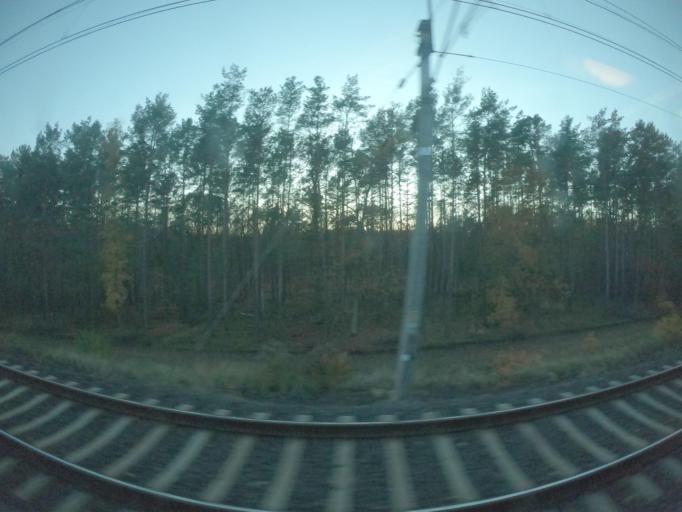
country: PL
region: West Pomeranian Voivodeship
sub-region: Powiat mysliborski
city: Boleszkowice
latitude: 52.7079
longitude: 14.5415
